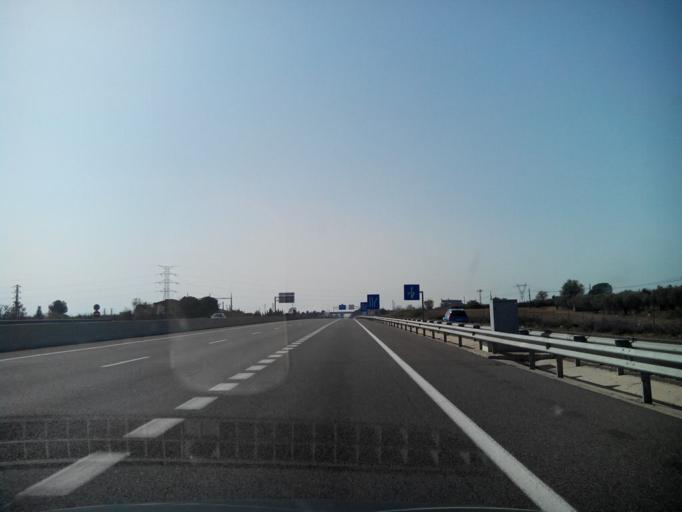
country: ES
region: Catalonia
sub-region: Provincia de Tarragona
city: La Selva
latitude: 41.2130
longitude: 1.1508
